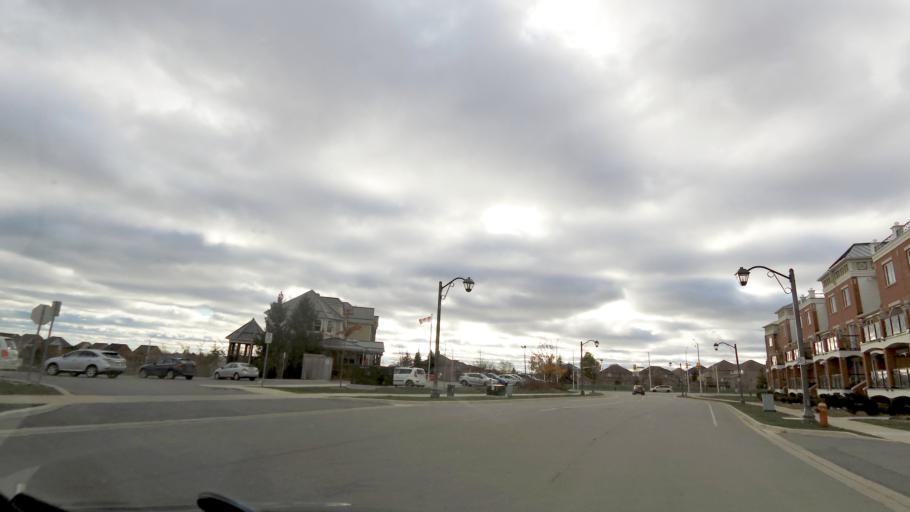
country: CA
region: Ontario
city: Oakville
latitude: 43.4783
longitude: -79.7260
